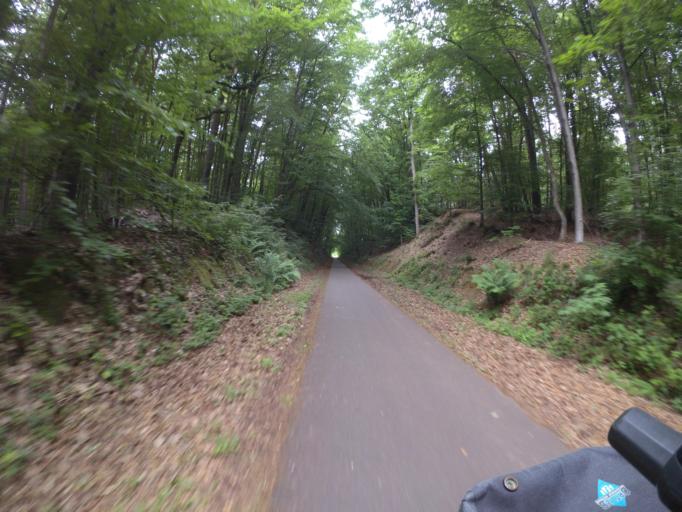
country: DE
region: Rheinland-Pfalz
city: Reichenbach-Steegen
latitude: 49.4889
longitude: 7.5640
